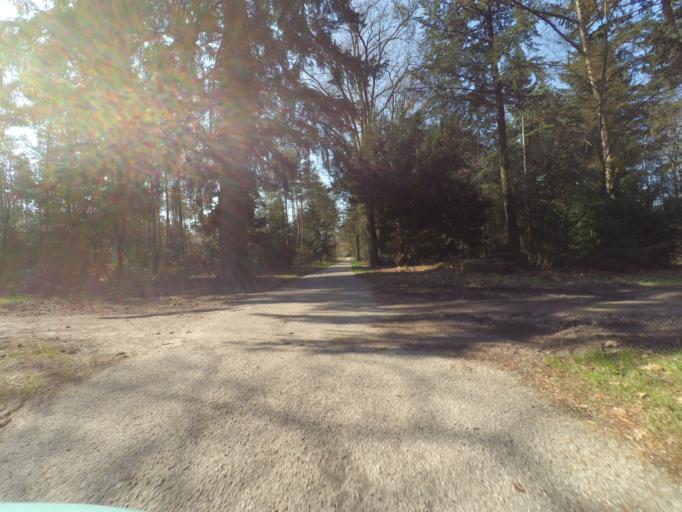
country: NL
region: Gelderland
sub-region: Gemeente Ede
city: Otterlo
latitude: 52.1043
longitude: 5.8402
